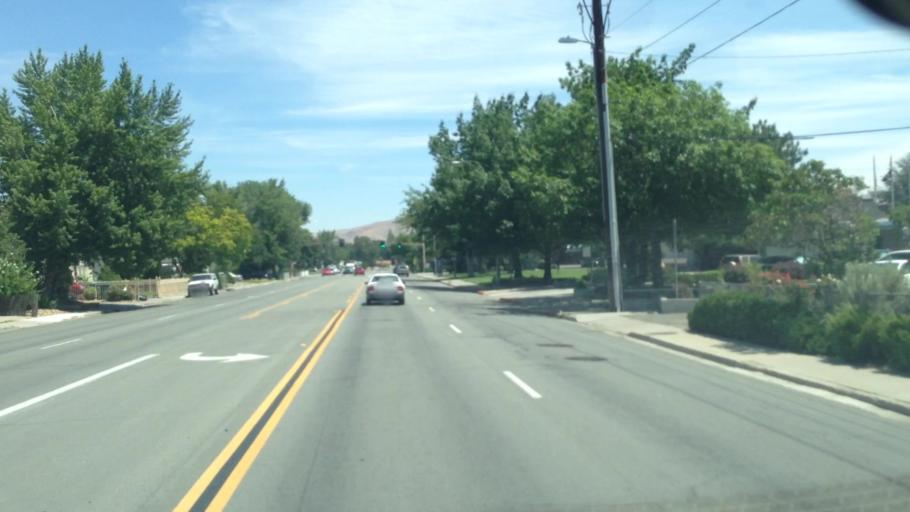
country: US
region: Nevada
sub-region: Washoe County
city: Sparks
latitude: 39.5408
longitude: -119.7501
